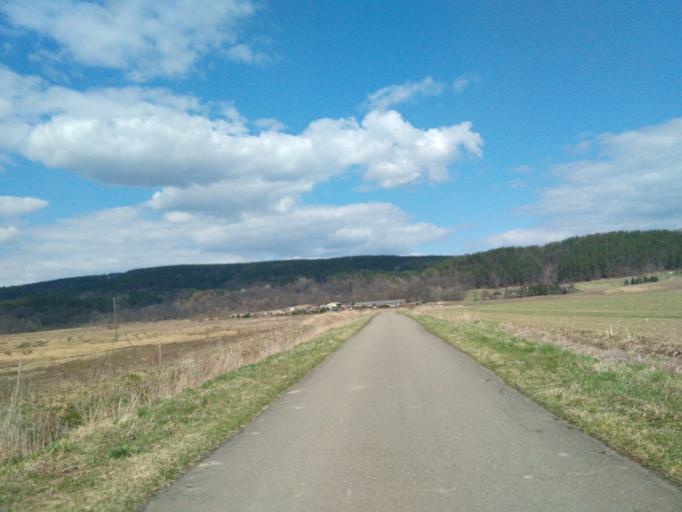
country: PL
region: Subcarpathian Voivodeship
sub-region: Powiat brzozowski
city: Dydnia
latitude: 49.6709
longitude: 22.2636
